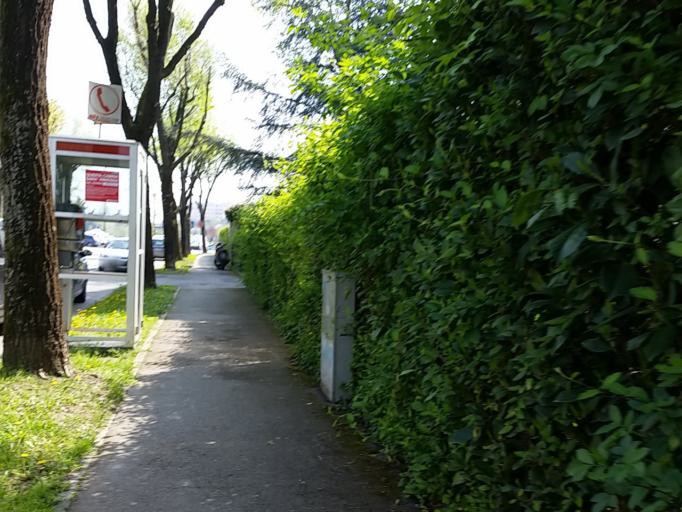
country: IT
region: Veneto
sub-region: Provincia di Padova
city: Mandriola-Sant'Agostino
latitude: 45.3780
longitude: 11.8612
